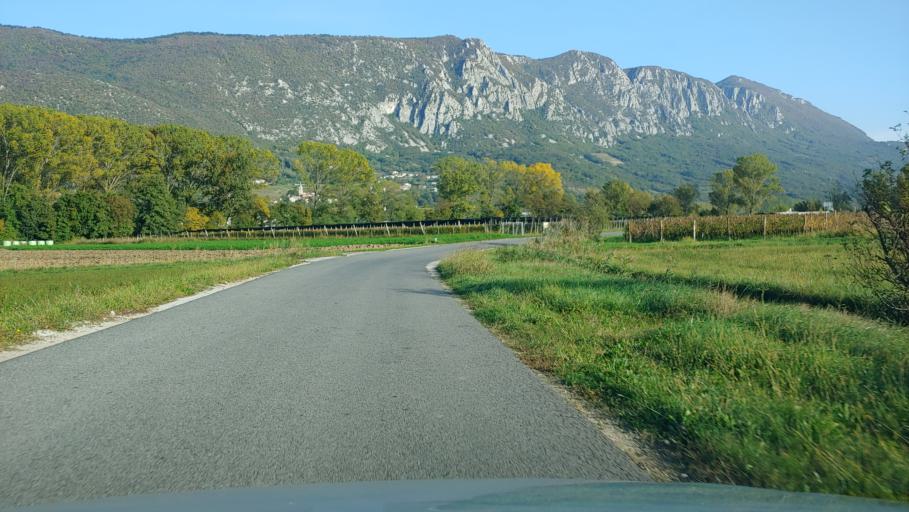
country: SI
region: Vipava
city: Vipava
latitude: 45.8376
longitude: 13.9467
